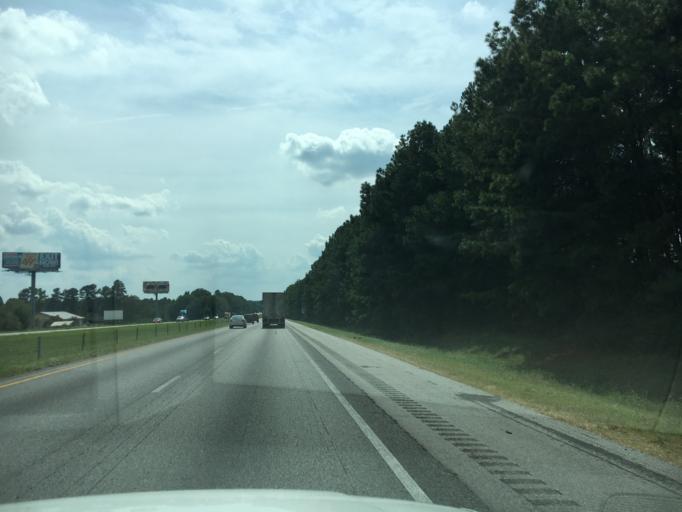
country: US
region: Georgia
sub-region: Franklin County
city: Lavonia
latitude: 34.4568
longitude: -83.1022
